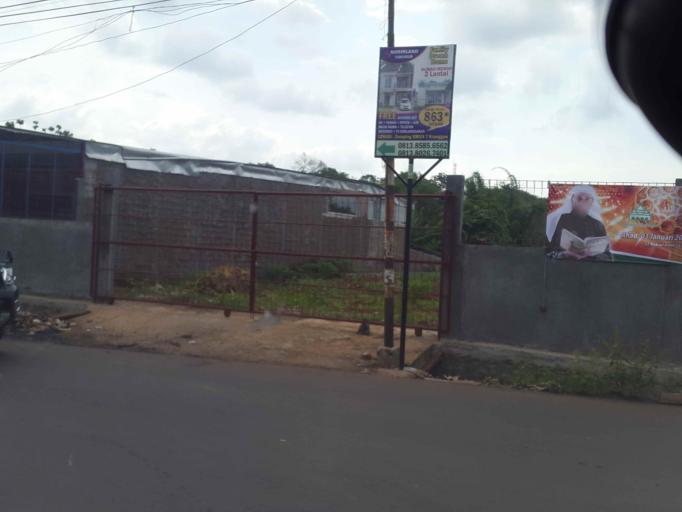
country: ID
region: West Java
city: Cileungsir
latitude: -6.3524
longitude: 106.9370
